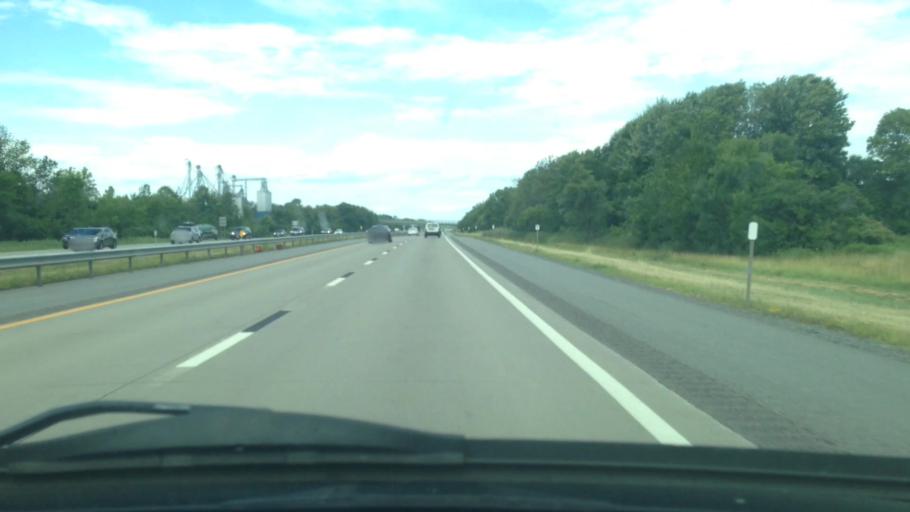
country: US
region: New York
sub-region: Onondaga County
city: Jordan
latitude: 43.0785
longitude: -76.4725
